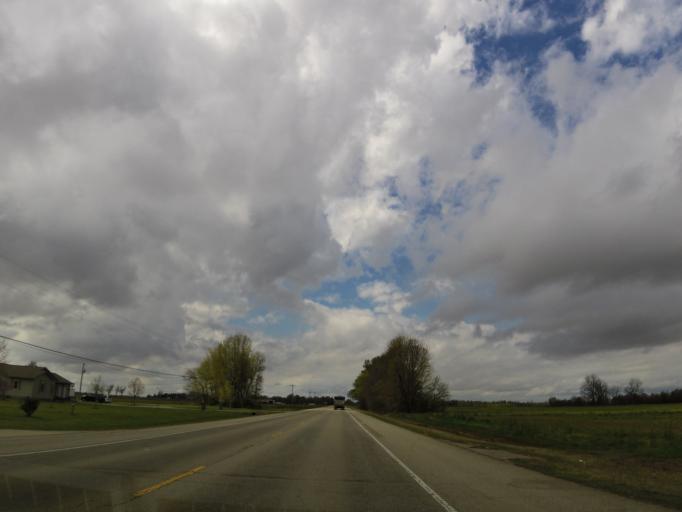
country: US
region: Arkansas
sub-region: Clay County
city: Corning
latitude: 36.4724
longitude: -90.5615
